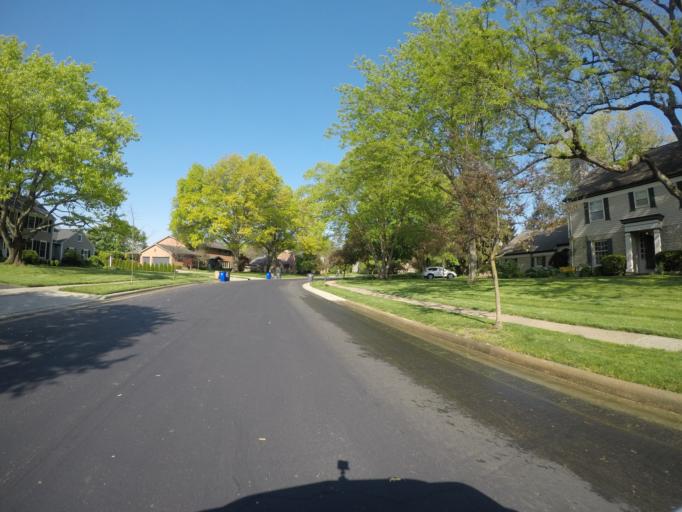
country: US
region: Ohio
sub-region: Franklin County
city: Upper Arlington
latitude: 40.0375
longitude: -83.0481
